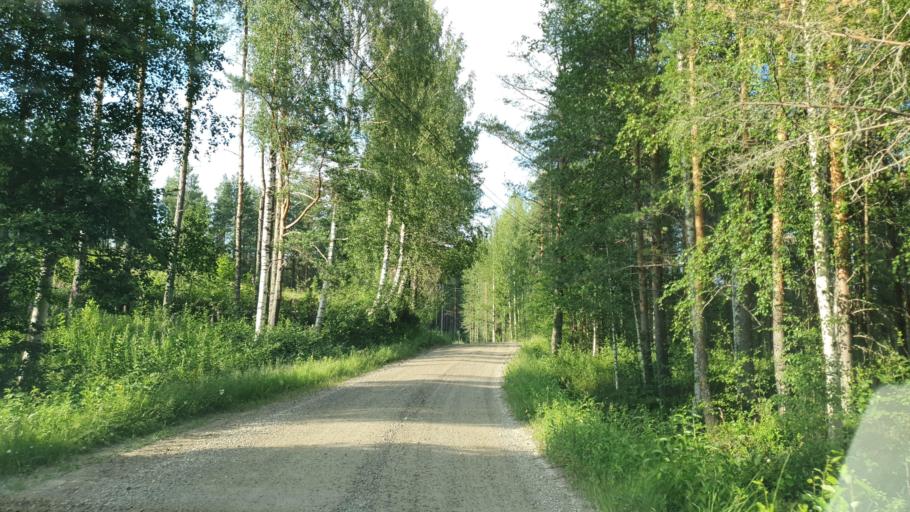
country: FI
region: Kainuu
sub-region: Kehys-Kainuu
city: Kuhmo
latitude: 64.3120
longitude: 29.5630
